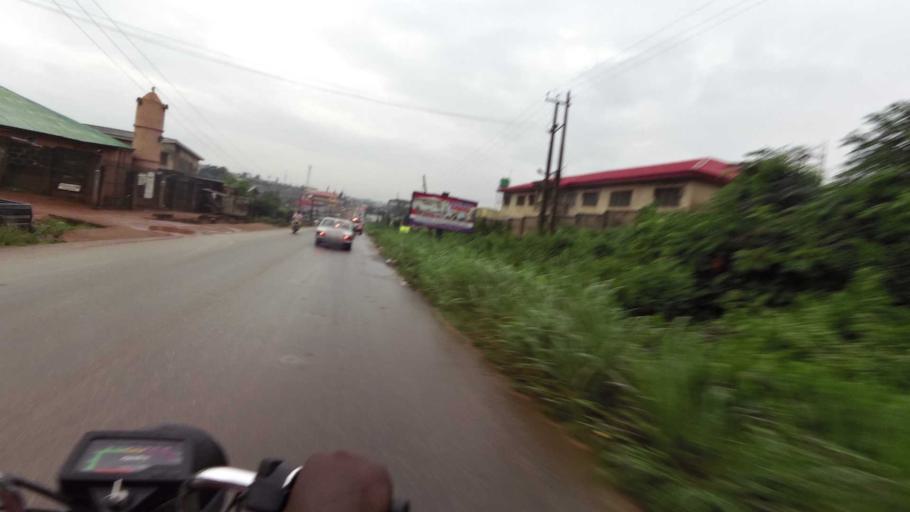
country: NG
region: Oyo
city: Ibadan
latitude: 7.4268
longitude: 3.9383
